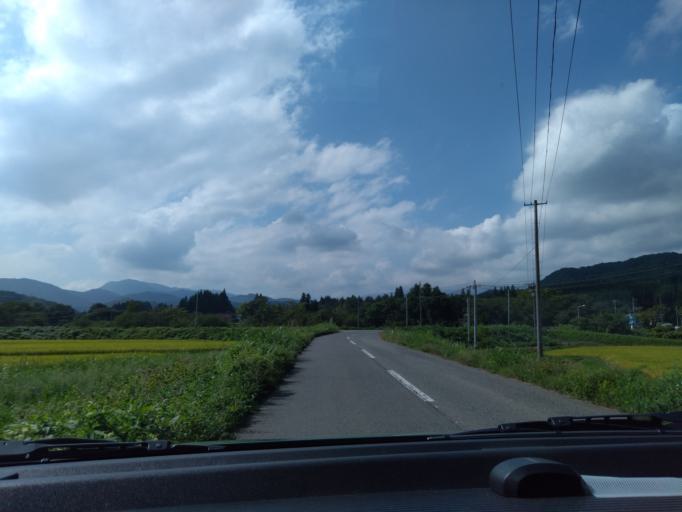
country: JP
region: Iwate
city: Shizukuishi
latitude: 39.6836
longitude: 140.9131
